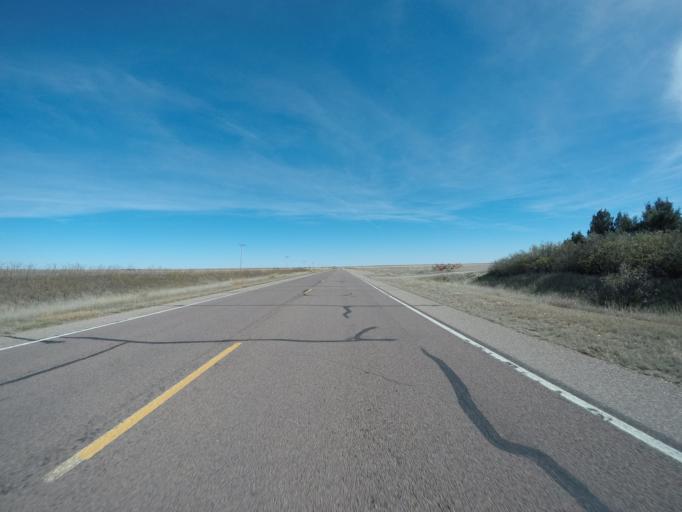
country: US
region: Colorado
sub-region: Kit Carson County
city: Burlington
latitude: 39.6581
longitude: -102.5350
